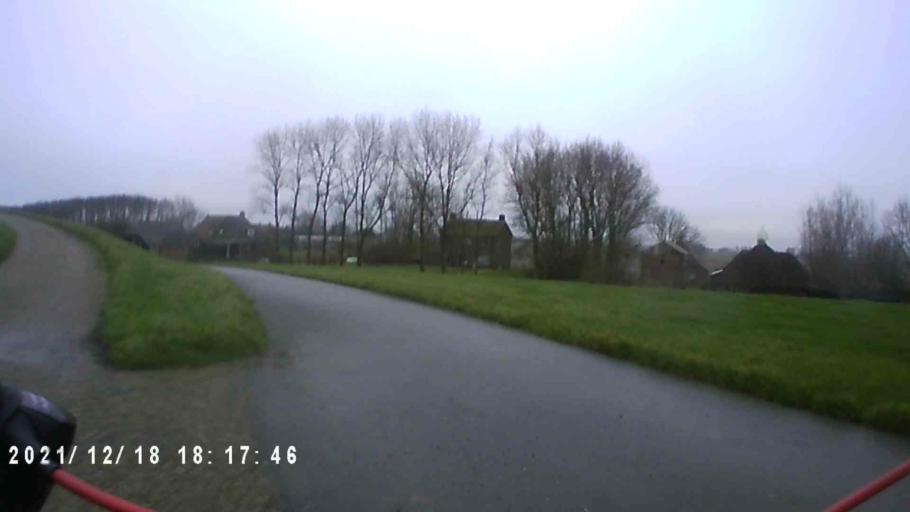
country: NL
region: Friesland
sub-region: Gemeente Dongeradeel
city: Ternaard
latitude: 53.3922
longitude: 5.9719
